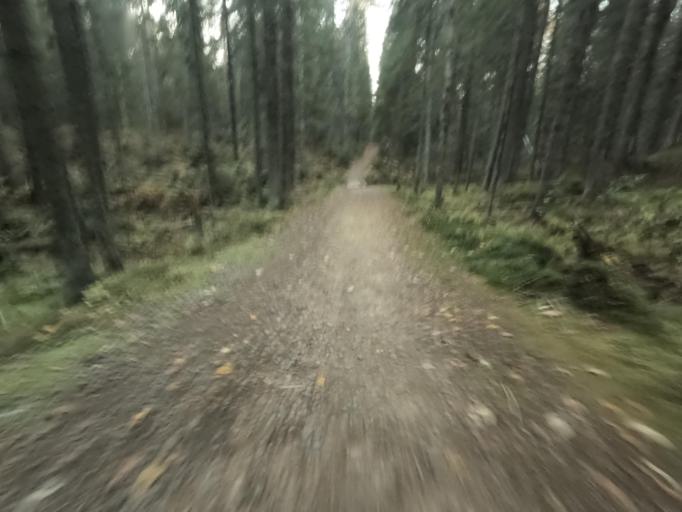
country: RU
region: Leningrad
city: Leninskoye
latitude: 60.1994
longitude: 29.8353
